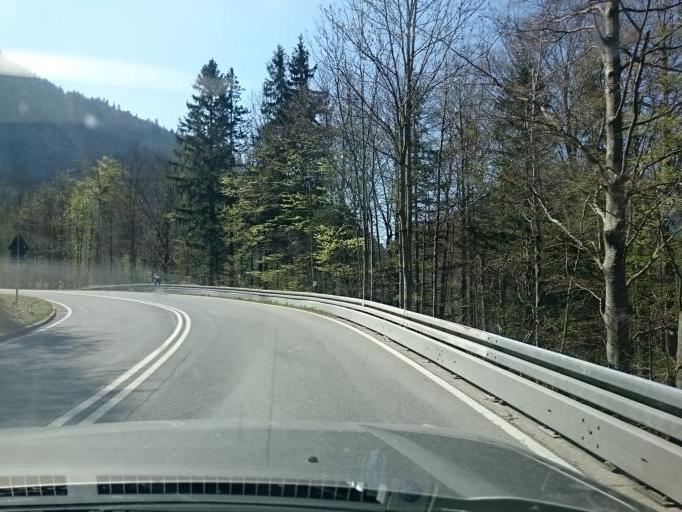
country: DE
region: Bavaria
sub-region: Upper Bavaria
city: Kochel
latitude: 47.6308
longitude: 11.3538
